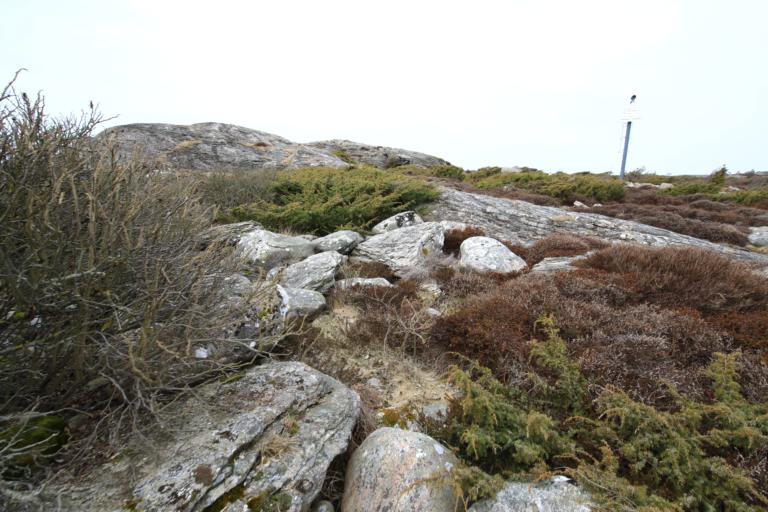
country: SE
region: Halland
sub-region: Kungsbacka Kommun
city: Frillesas
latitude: 57.2461
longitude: 12.1004
